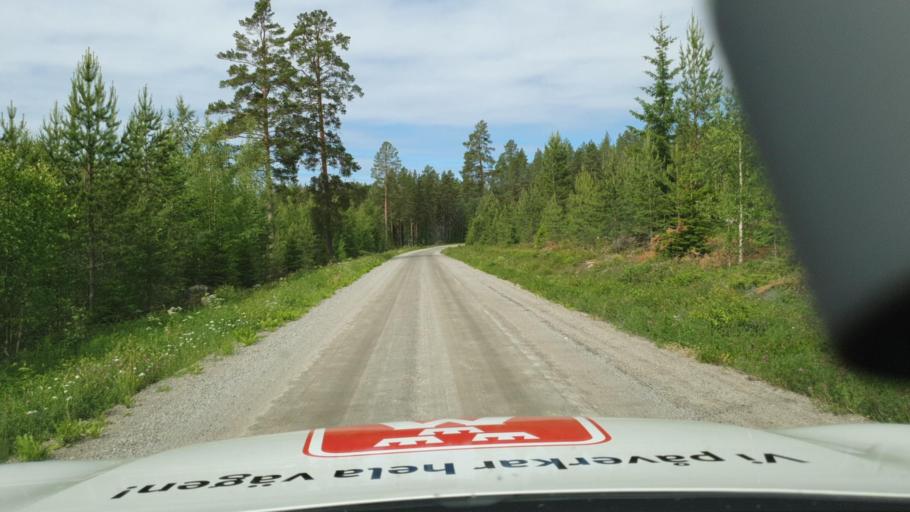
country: SE
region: Vaesterbotten
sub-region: Skelleftea Kommun
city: Burtraesk
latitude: 64.6169
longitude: 20.5769
